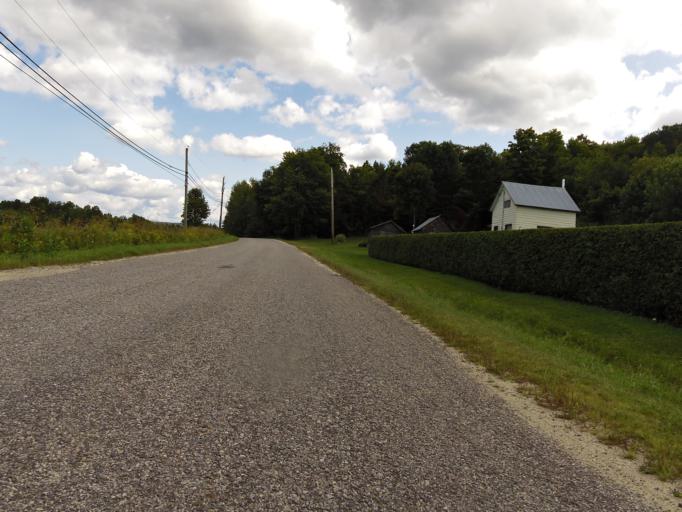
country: CA
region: Quebec
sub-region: Outaouais
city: Wakefield
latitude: 45.8045
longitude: -75.9781
